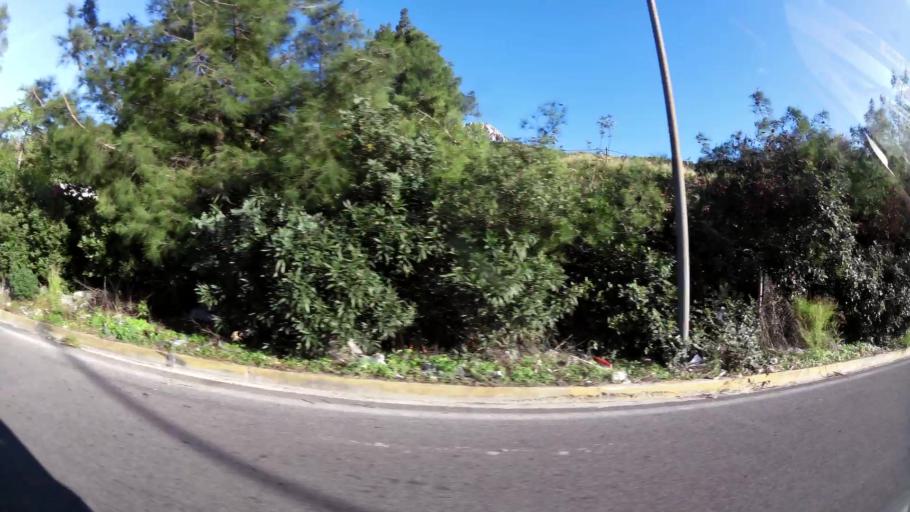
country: GR
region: Attica
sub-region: Nomarchia Athinas
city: Skaramangas
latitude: 38.0022
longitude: 23.6028
